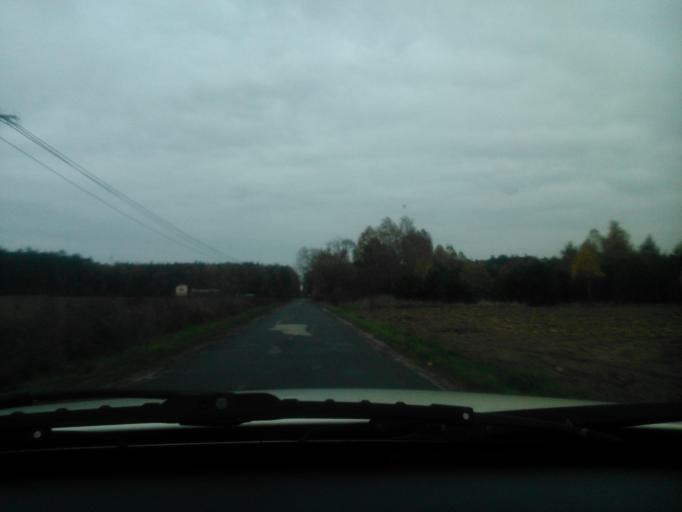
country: PL
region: Kujawsko-Pomorskie
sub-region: Powiat golubsko-dobrzynski
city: Golub-Dobrzyn
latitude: 53.1366
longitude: 19.1034
